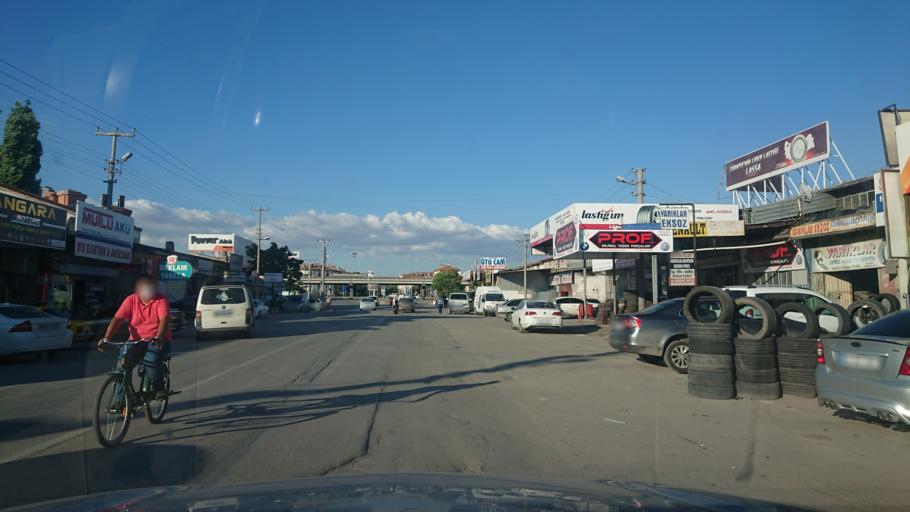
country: TR
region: Aksaray
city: Aksaray
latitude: 38.3742
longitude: 33.9983
